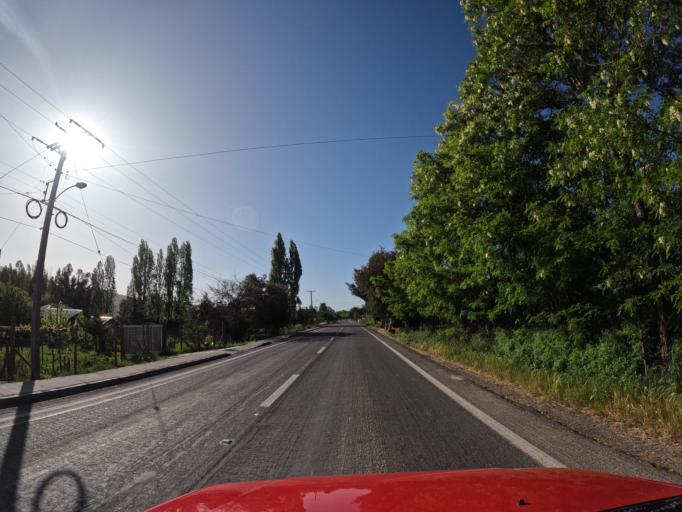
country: CL
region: Maule
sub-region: Provincia de Curico
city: Teno
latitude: -34.7946
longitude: -71.2266
